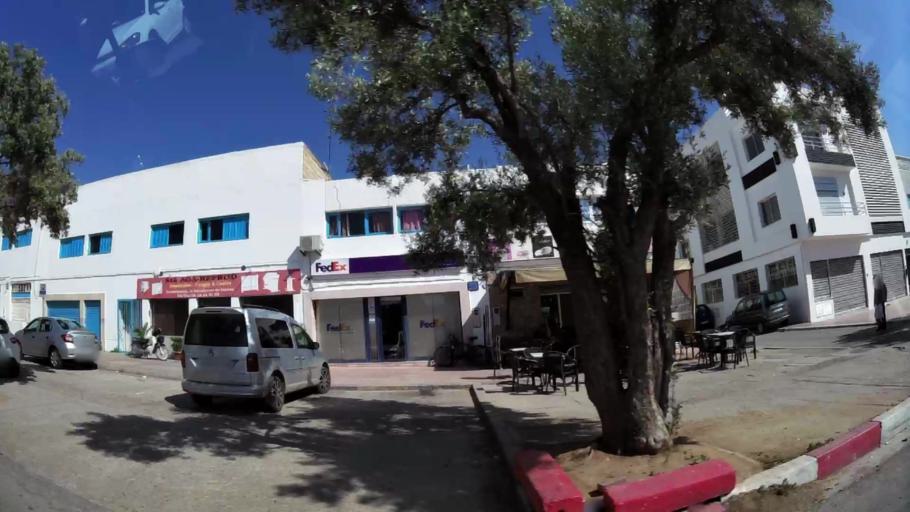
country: MA
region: Souss-Massa-Draa
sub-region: Agadir-Ida-ou-Tnan
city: Agadir
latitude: 30.4235
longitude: -9.5970
